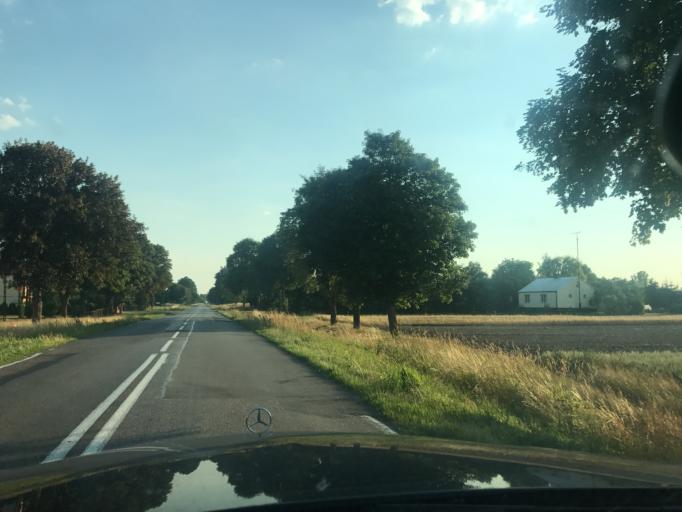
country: PL
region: Lublin Voivodeship
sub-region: Powiat bialski
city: Wisznice
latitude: 51.7584
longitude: 23.1784
